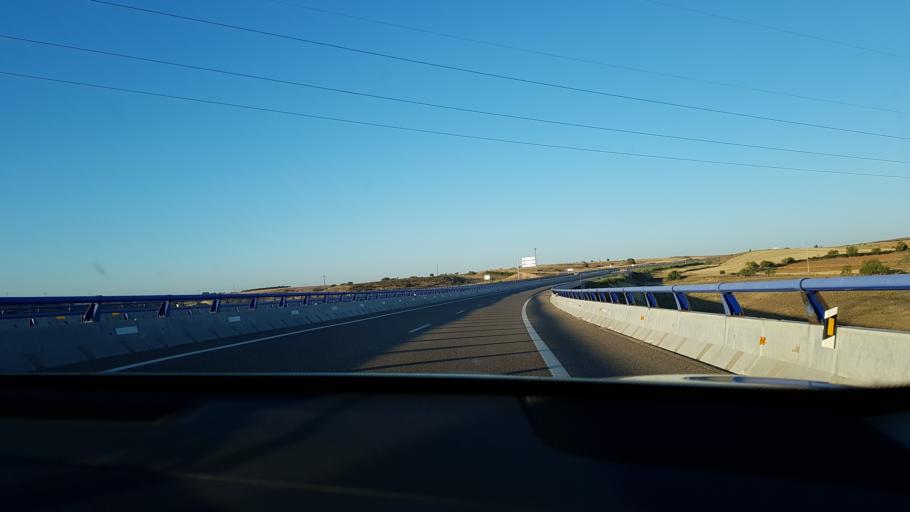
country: ES
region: Castille and Leon
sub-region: Provincia de Zamora
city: Roales
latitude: 41.5346
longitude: -5.7745
